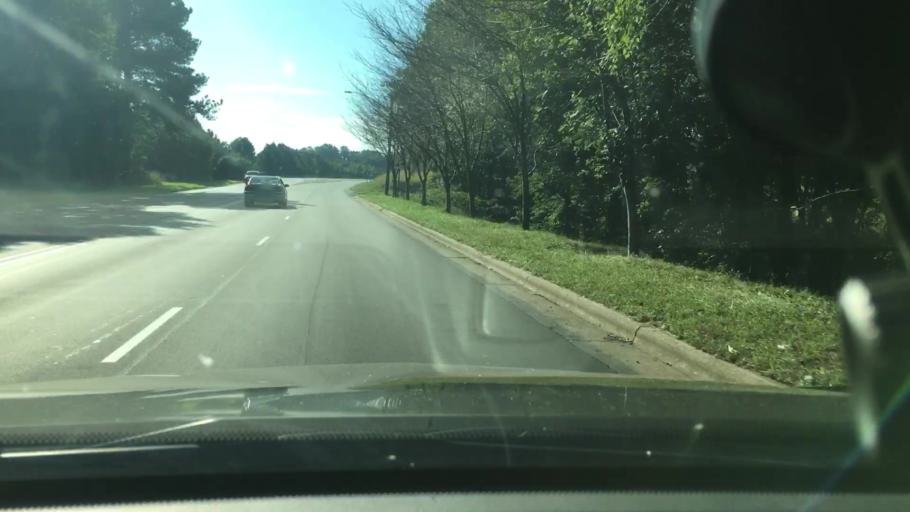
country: US
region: North Carolina
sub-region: Stanly County
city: Albemarle
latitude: 35.3432
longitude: -80.2024
